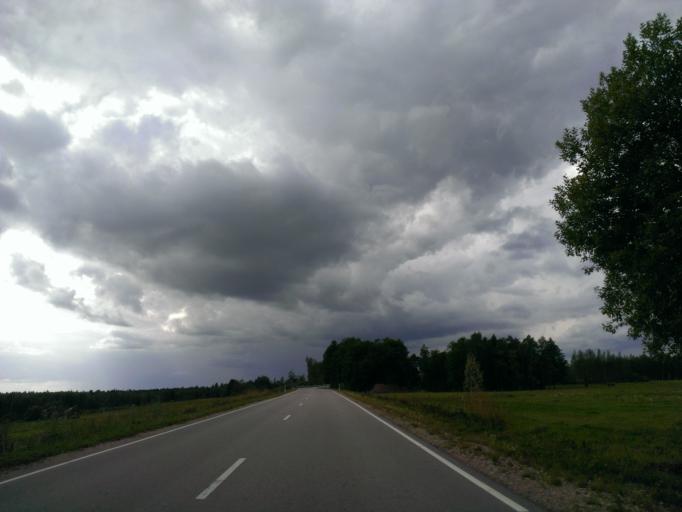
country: LV
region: Malpils
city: Malpils
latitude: 56.8956
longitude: 25.1445
